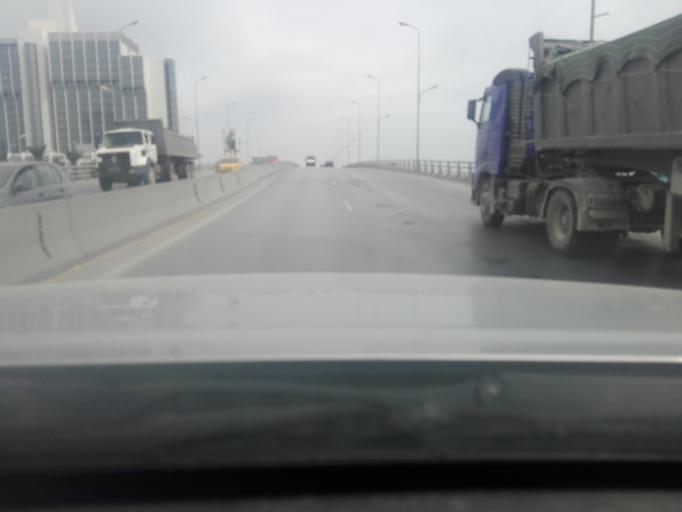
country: TN
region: Tunis
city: Tunis
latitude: 36.8056
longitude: 10.1886
